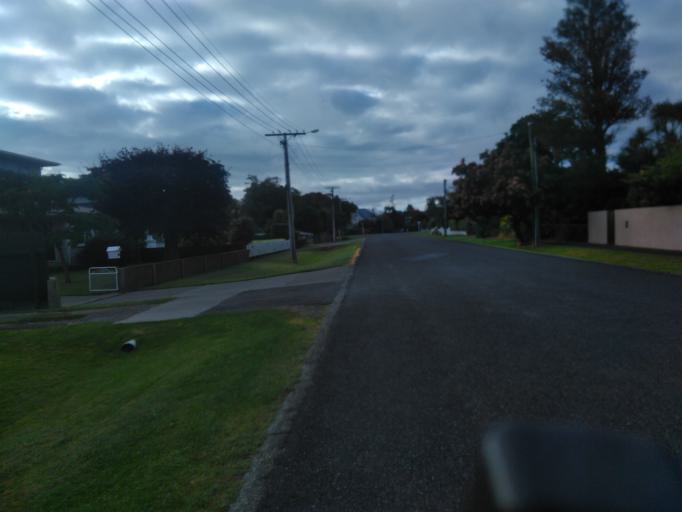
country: NZ
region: Gisborne
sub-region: Gisborne District
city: Gisborne
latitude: -38.6597
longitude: 178.0309
